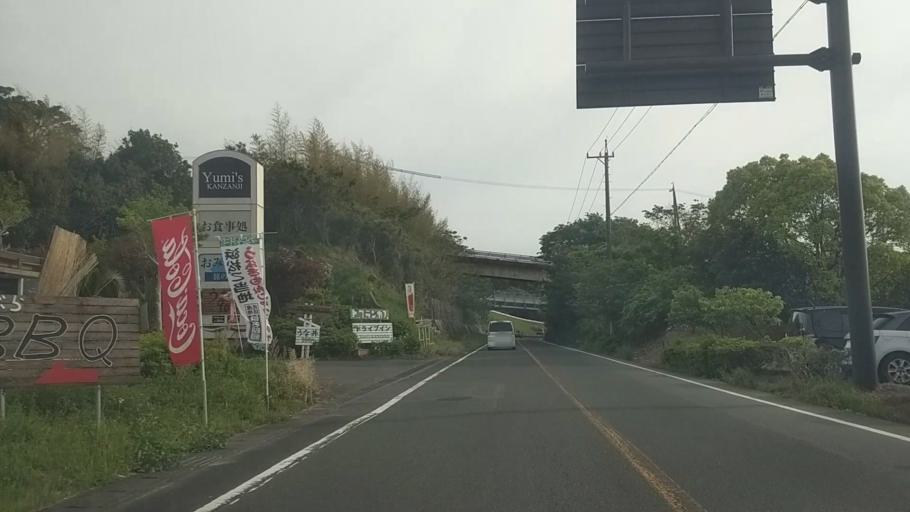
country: JP
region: Shizuoka
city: Kosai-shi
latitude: 34.7614
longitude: 137.6184
